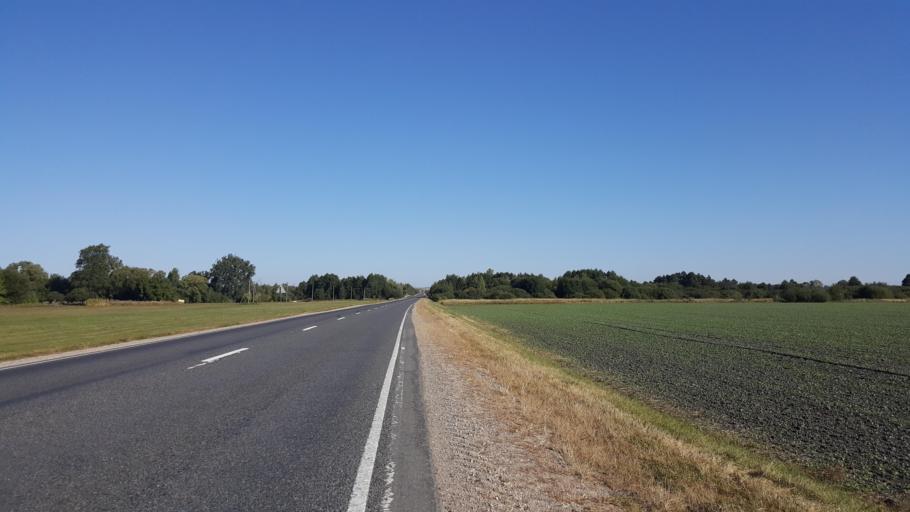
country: BY
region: Brest
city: Kamyanyets
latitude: 52.3827
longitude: 23.7883
